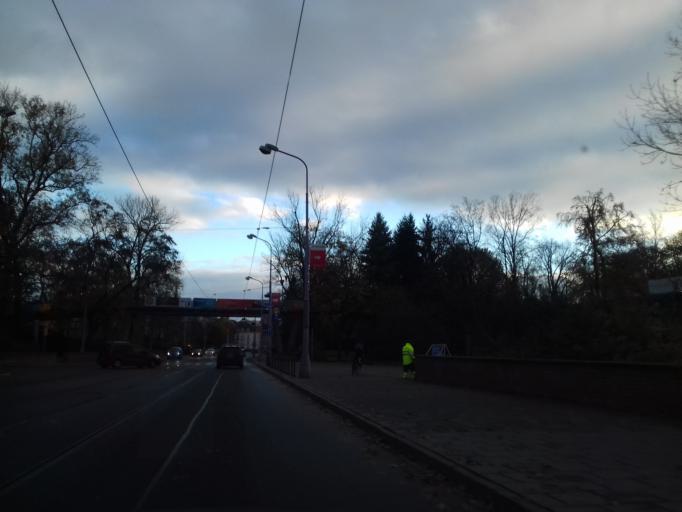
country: CZ
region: Olomoucky
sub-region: Okres Olomouc
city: Olomouc
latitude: 49.5897
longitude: 17.2459
